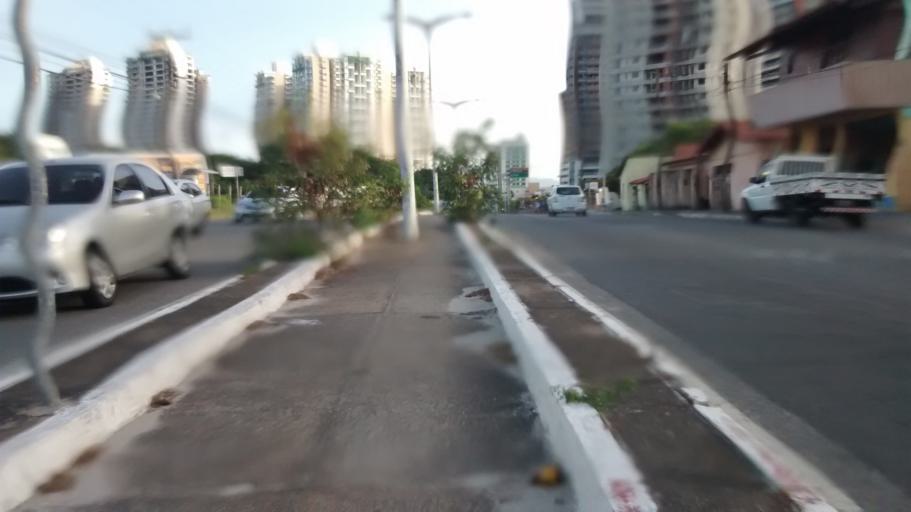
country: BR
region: Ceara
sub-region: Fortaleza
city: Fortaleza
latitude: -3.7627
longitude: -38.4940
